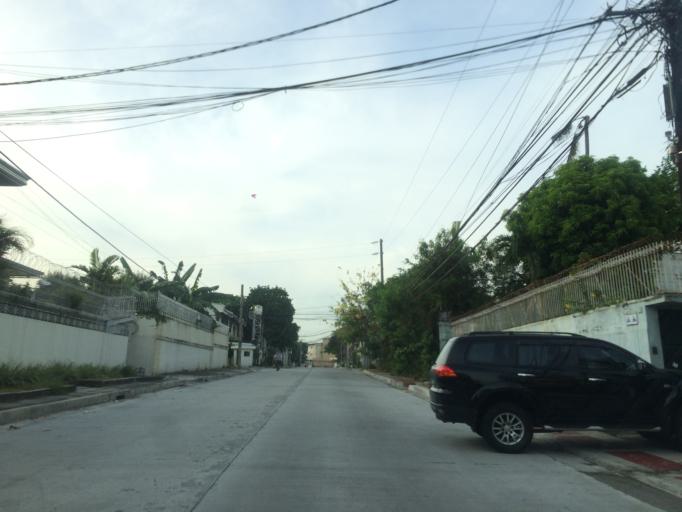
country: PH
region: Calabarzon
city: Del Monte
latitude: 14.6305
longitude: 121.0056
